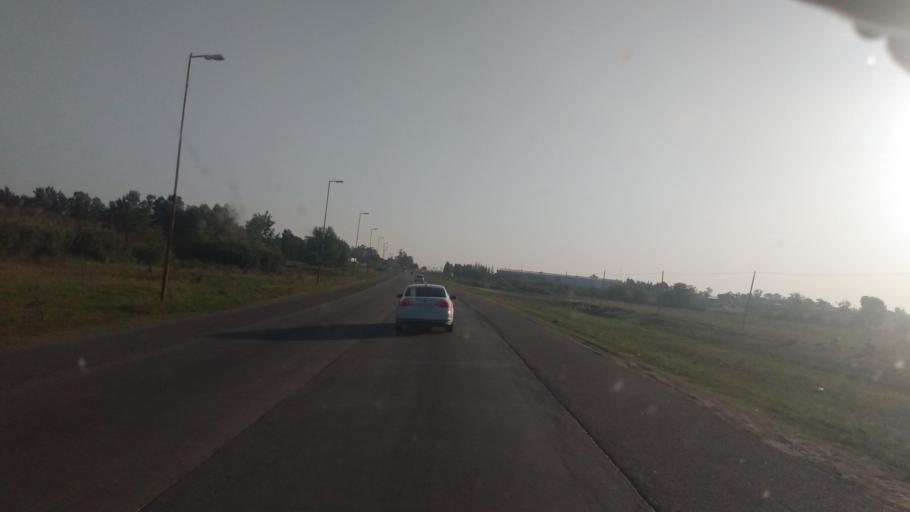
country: AR
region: Buenos Aires
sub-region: Partido de Campana
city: Campana
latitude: -34.1945
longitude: -58.9515
